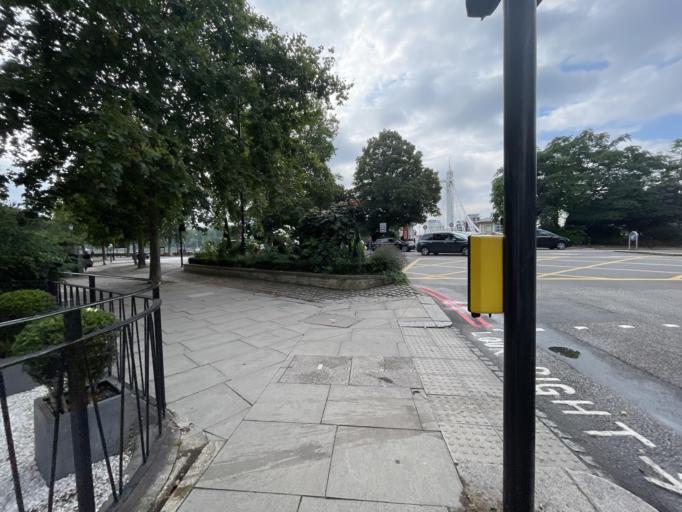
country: GB
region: England
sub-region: Greater London
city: Chelsea
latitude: 51.4837
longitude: -0.1673
